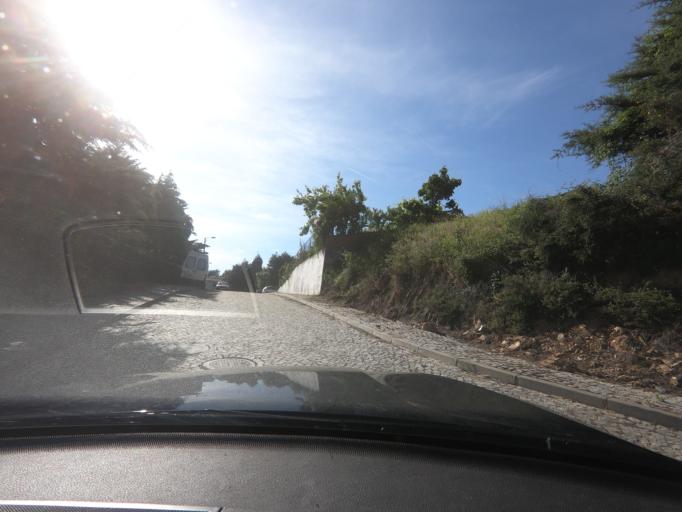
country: PT
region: Vila Real
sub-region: Vila Real
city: Vila Real
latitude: 41.2987
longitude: -7.7099
